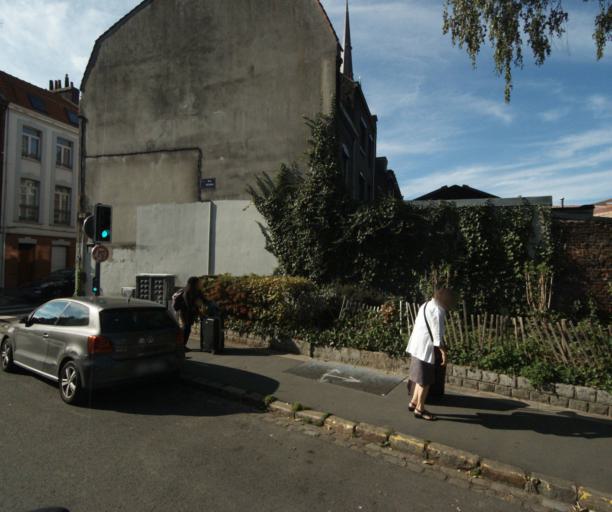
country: FR
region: Nord-Pas-de-Calais
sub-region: Departement du Nord
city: La Madeleine
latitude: 50.6334
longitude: 3.0883
